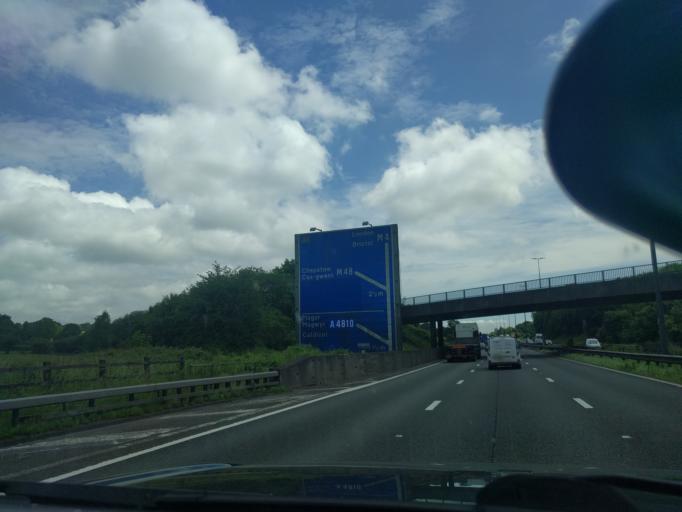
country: GB
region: Wales
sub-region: Newport
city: Bishton
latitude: 51.5988
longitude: -2.8811
